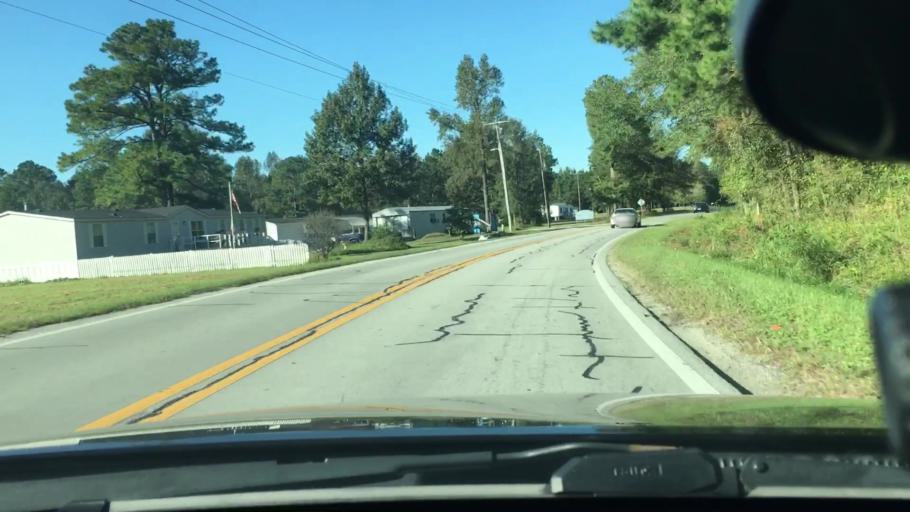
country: US
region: North Carolina
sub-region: Craven County
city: Vanceboro
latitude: 35.2304
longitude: -77.1365
